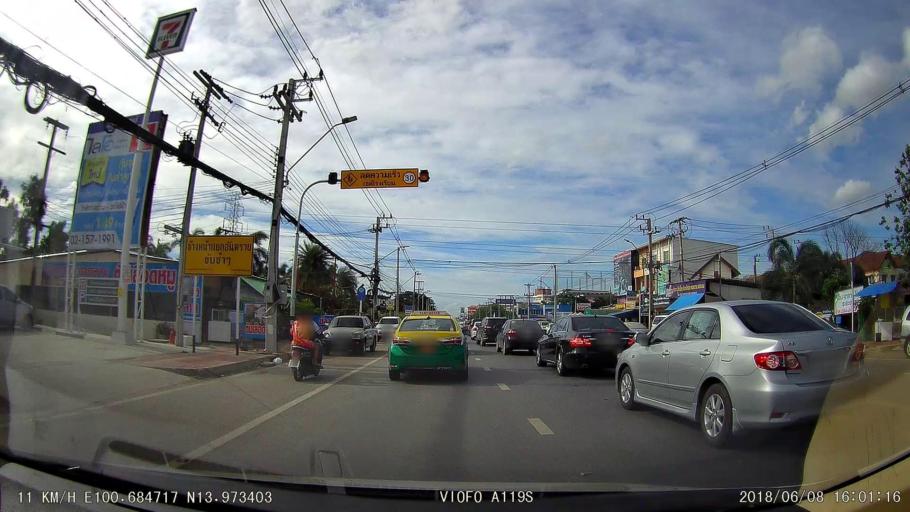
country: TH
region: Bangkok
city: Sai Mai
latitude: 13.9734
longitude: 100.6847
